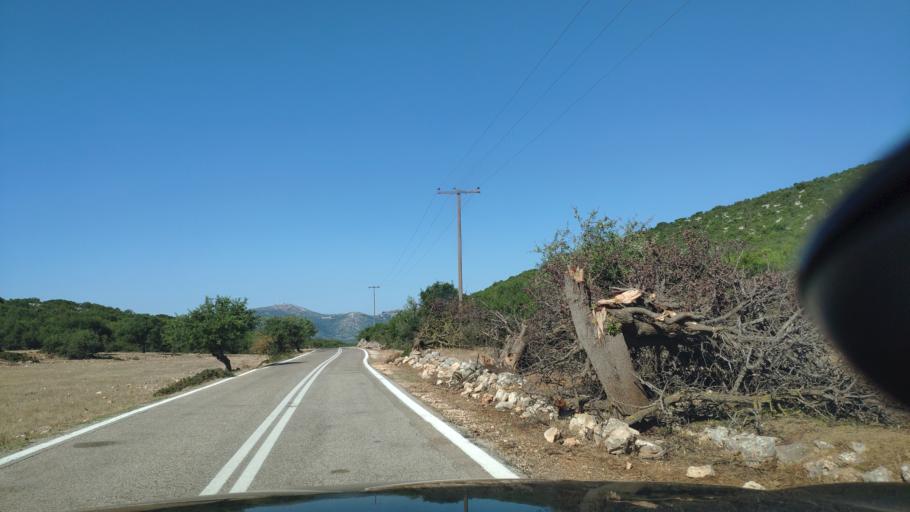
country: GR
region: West Greece
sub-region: Nomos Aitolias kai Akarnanias
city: Archontochorion
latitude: 38.6901
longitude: 21.0741
